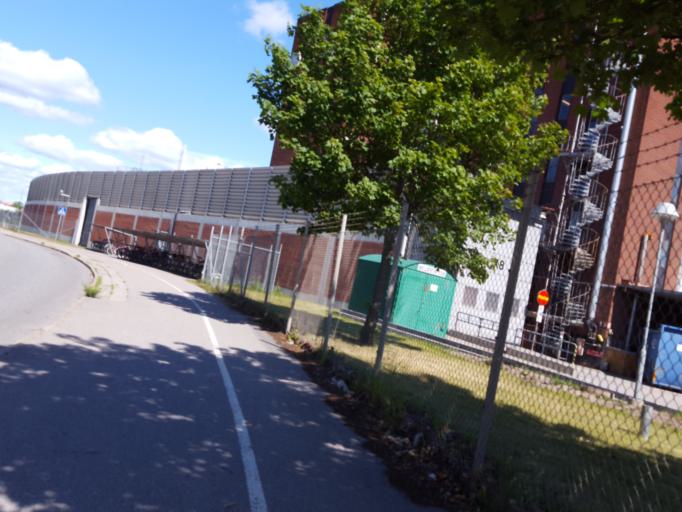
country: SE
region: Uppsala
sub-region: Uppsala Kommun
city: Uppsala
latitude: 59.8506
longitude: 17.6672
